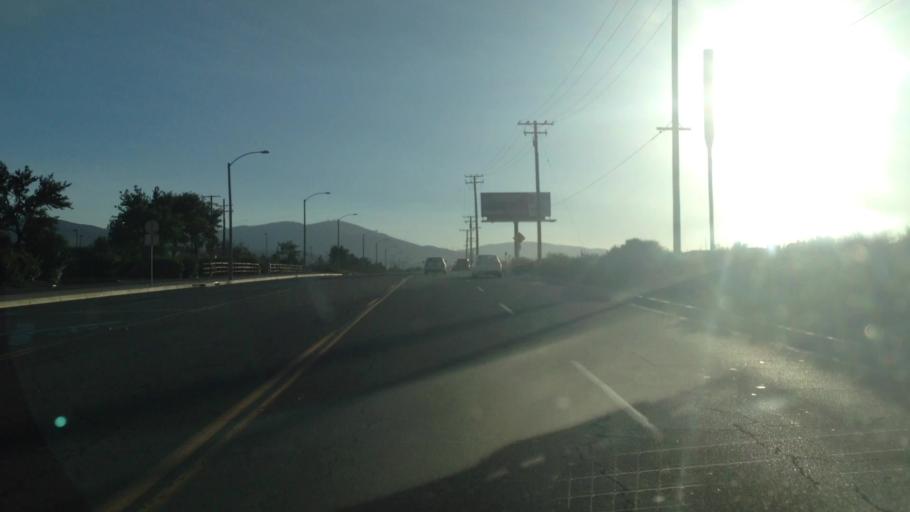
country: US
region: California
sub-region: Los Angeles County
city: Palmdale
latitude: 34.5581
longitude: -118.1159
